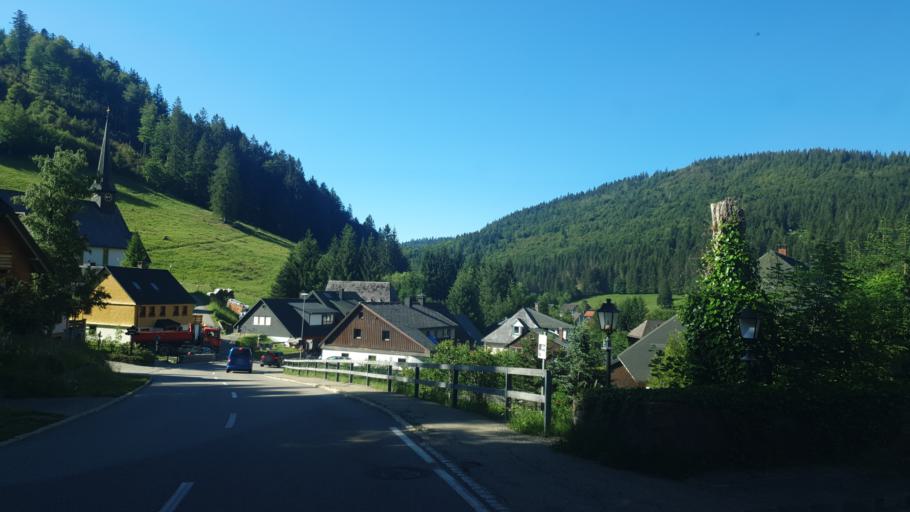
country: DE
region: Baden-Wuerttemberg
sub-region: Freiburg Region
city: Todtnau
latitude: 47.8590
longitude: 7.9182
